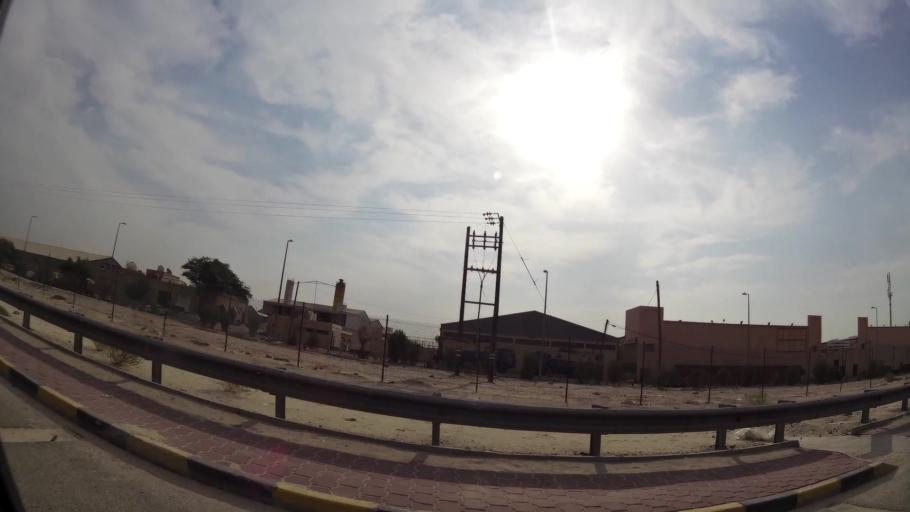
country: KW
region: Muhafazat al Jahra'
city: Al Jahra'
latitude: 29.2998
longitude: 47.7373
